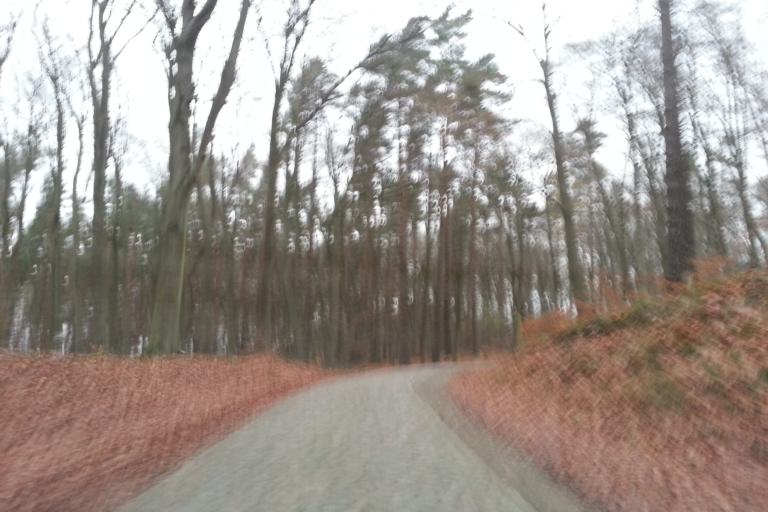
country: DE
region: Mecklenburg-Vorpommern
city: Ferdinandshof
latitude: 53.5908
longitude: 13.8413
